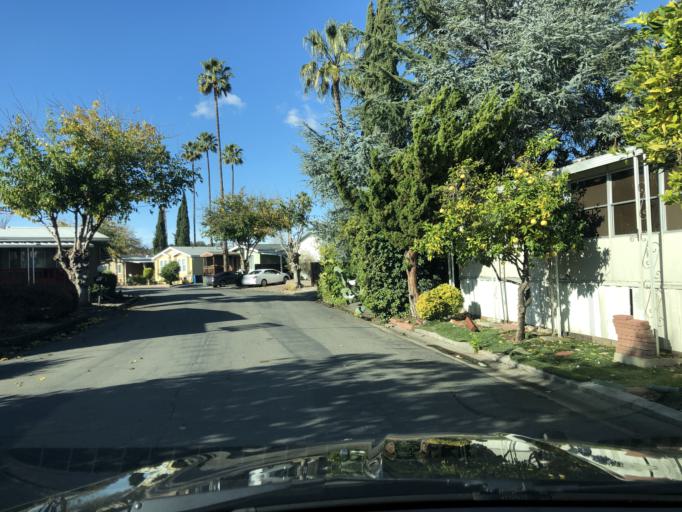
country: US
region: California
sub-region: Contra Costa County
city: Pacheco
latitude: 37.9874
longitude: -122.0649
